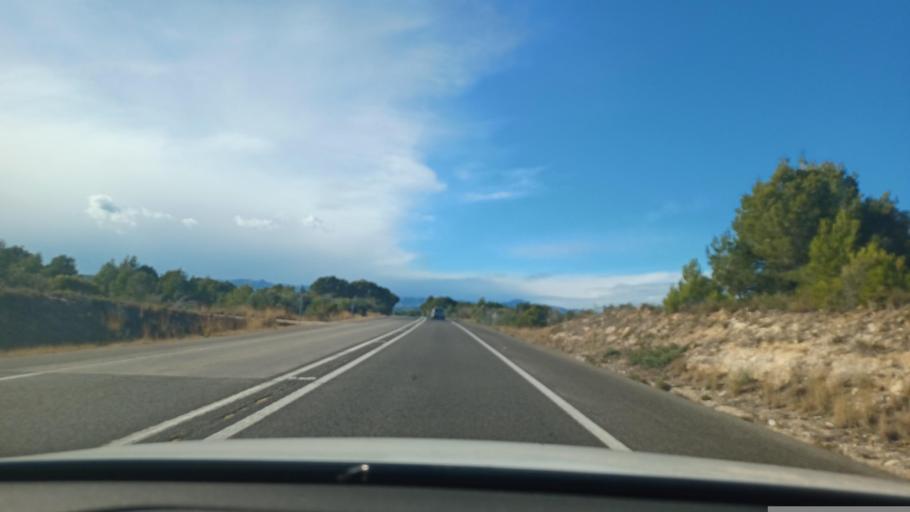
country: ES
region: Catalonia
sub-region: Provincia de Tarragona
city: l'Ametlla de Mar
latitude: 40.8940
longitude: 0.7751
